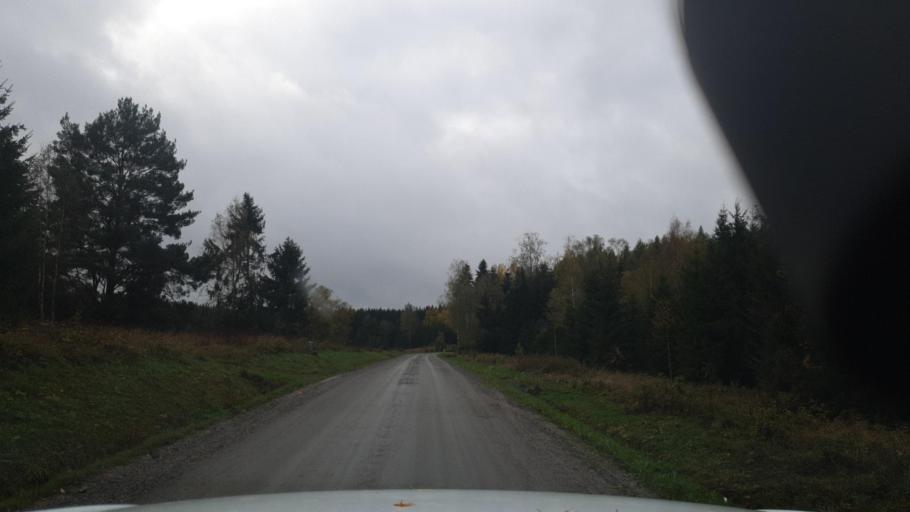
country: SE
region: Vaermland
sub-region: Karlstads Kommun
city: Edsvalla
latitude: 59.5488
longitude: 13.0093
